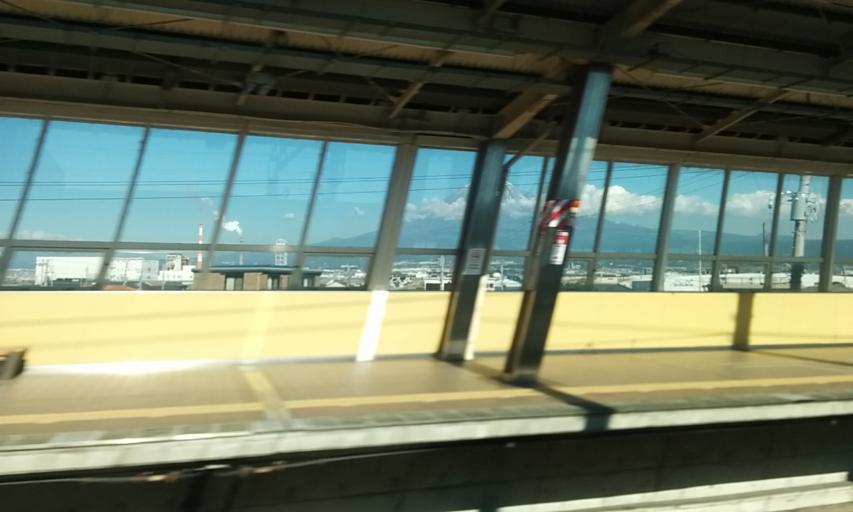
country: JP
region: Shizuoka
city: Fuji
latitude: 35.1427
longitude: 138.6643
